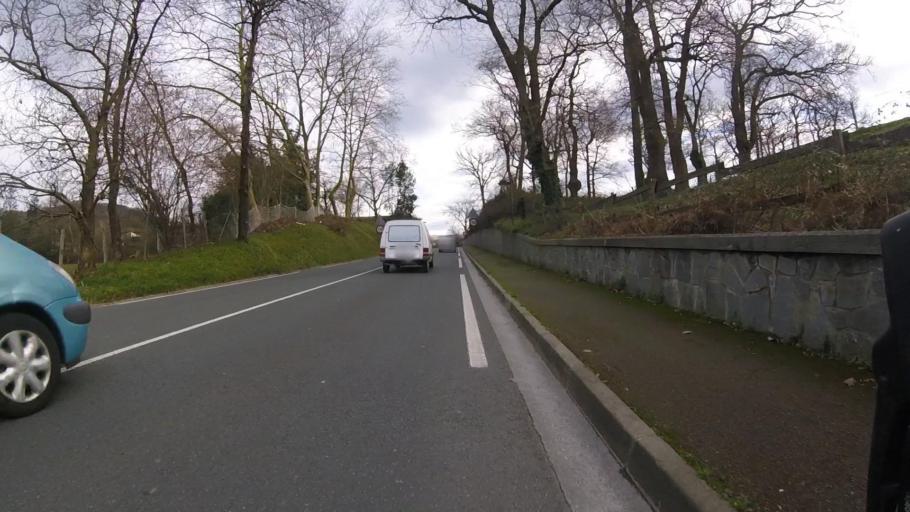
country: ES
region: Basque Country
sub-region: Provincia de Guipuzcoa
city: Lezo
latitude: 43.3047
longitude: -1.8762
